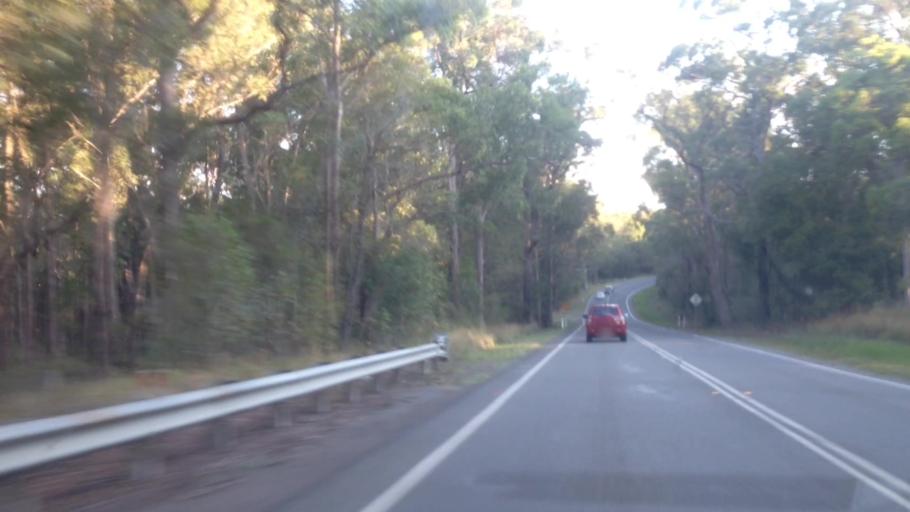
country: AU
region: New South Wales
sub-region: Lake Macquarie Shire
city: Dora Creek
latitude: -32.9986
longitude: 151.4926
